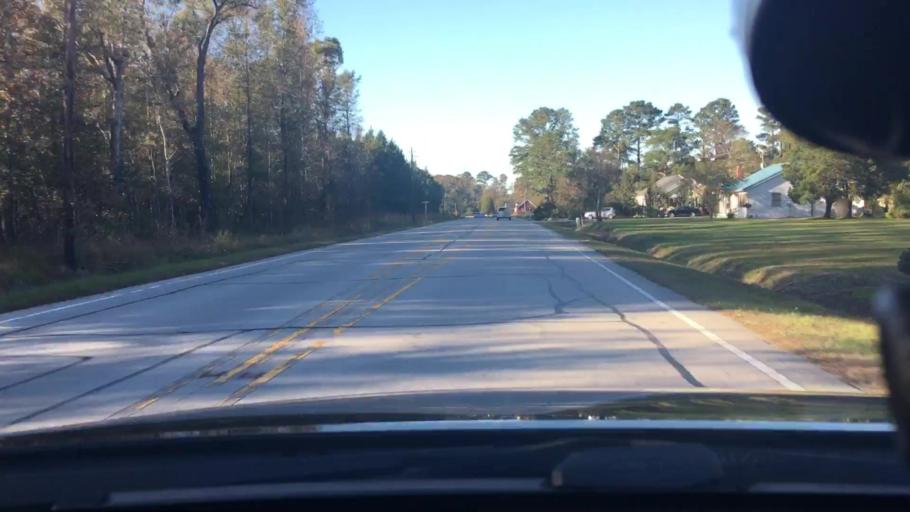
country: US
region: North Carolina
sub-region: Craven County
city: Vanceboro
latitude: 35.3315
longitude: -77.1715
